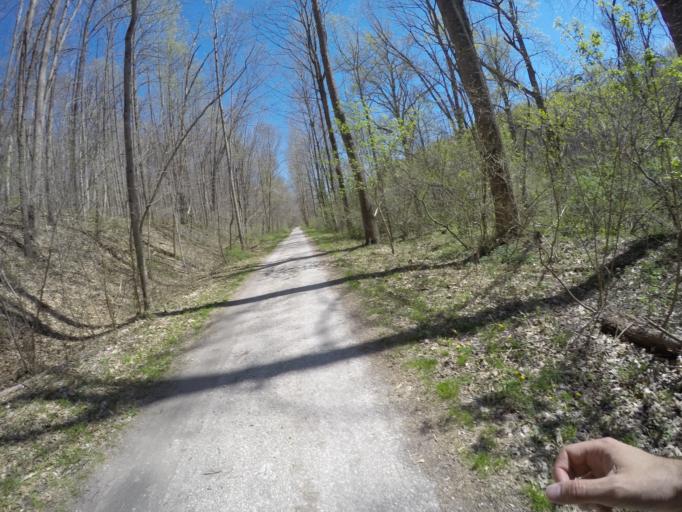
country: US
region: Maryland
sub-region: Baltimore County
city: Hunt Valley
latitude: 39.5928
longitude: -76.6199
